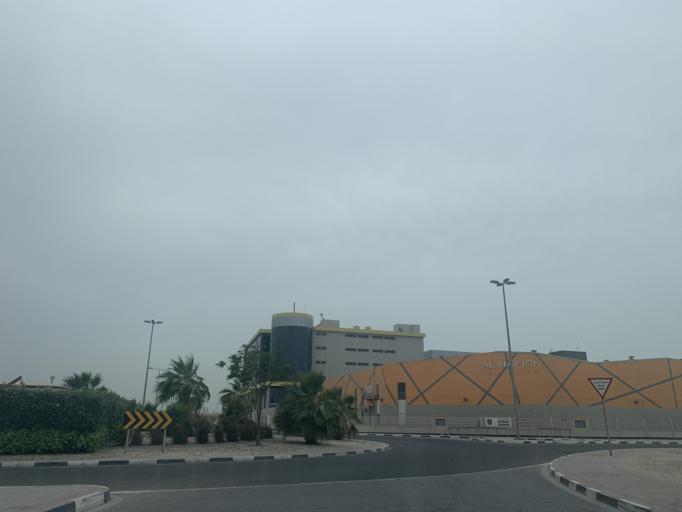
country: BH
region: Muharraq
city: Al Hadd
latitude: 26.2134
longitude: 50.6733
